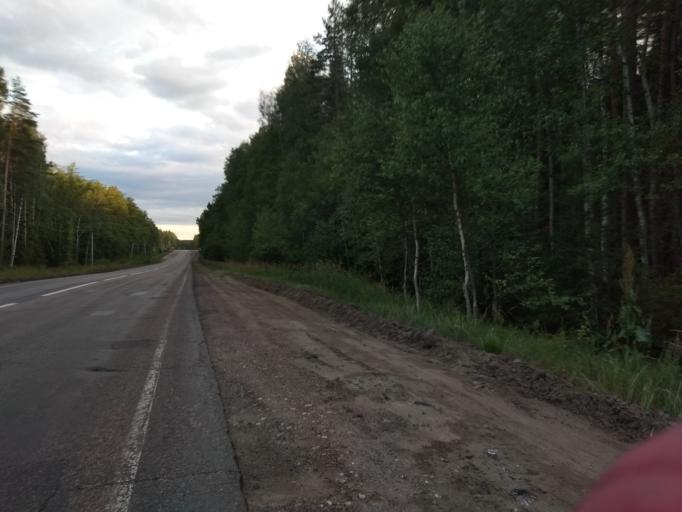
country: RU
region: Moskovskaya
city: Misheronskiy
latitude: 55.6372
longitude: 39.7496
